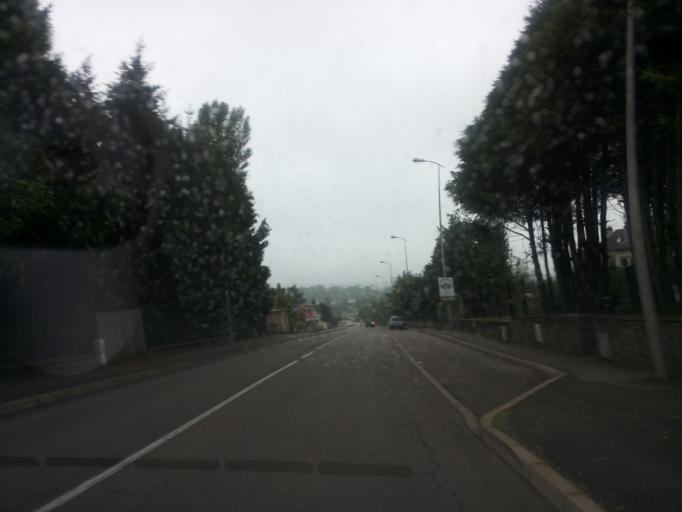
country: FR
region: Lorraine
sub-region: Departement des Vosges
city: Epinal
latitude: 48.1767
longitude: 6.4778
